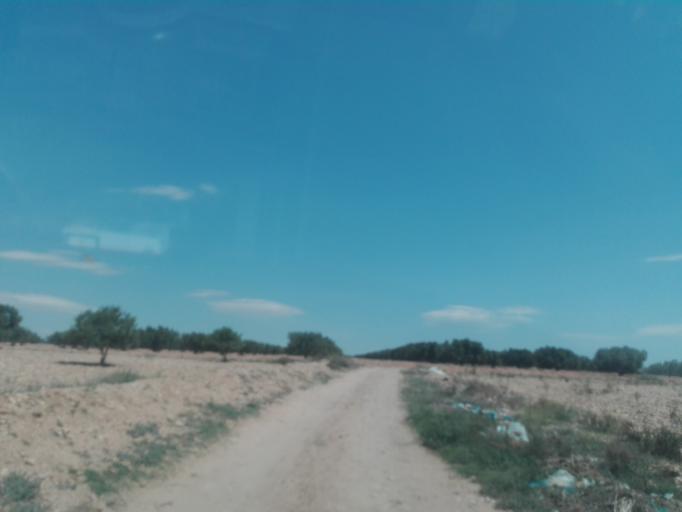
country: TN
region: Safaqis
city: Sfax
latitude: 34.6579
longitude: 10.5984
